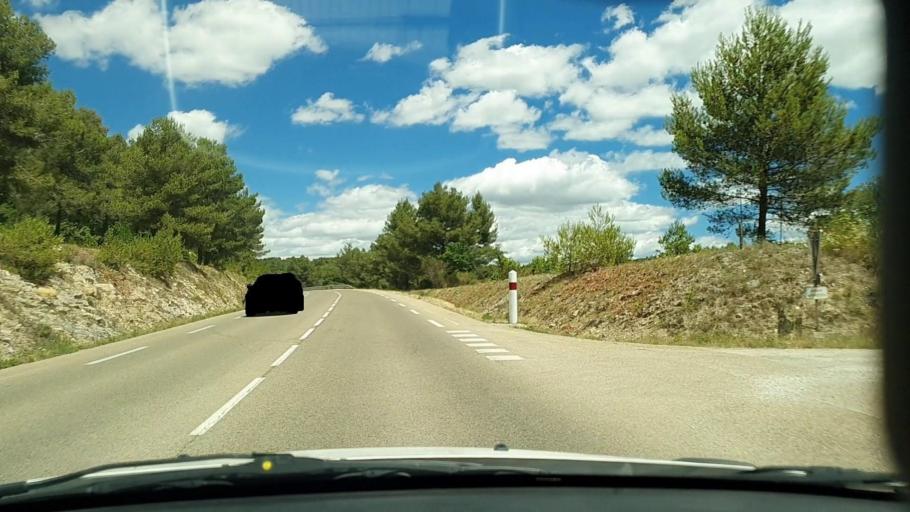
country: FR
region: Languedoc-Roussillon
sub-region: Departement du Gard
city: Poulx
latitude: 43.8782
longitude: 4.4164
